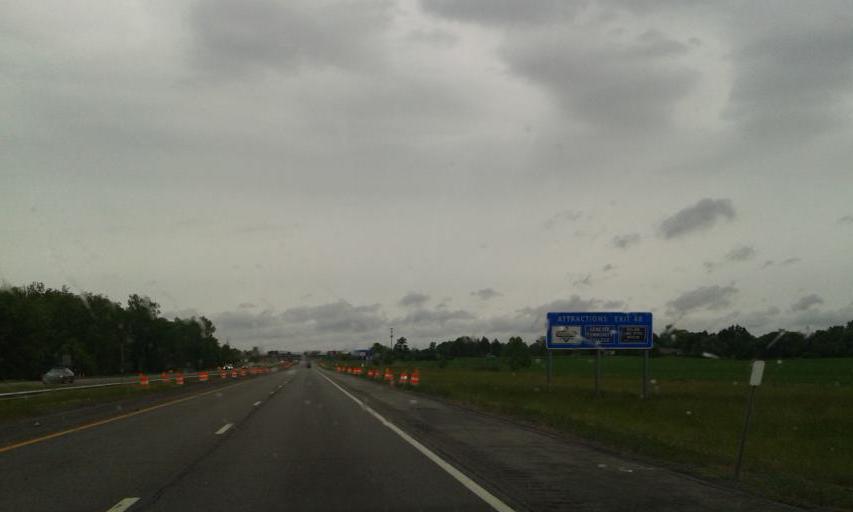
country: US
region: New York
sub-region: Genesee County
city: Batavia
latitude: 43.0201
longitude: -78.1695
